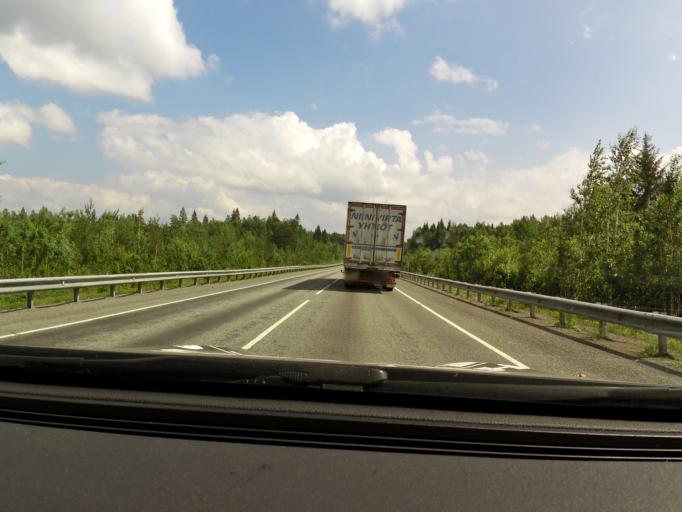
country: RU
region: Sverdlovsk
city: Achit
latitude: 56.8326
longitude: 57.7788
